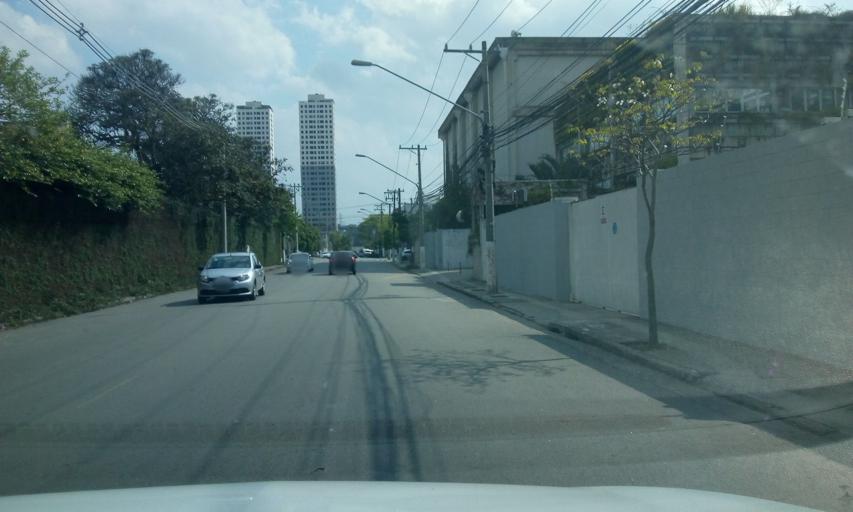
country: BR
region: Sao Paulo
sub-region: Osasco
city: Osasco
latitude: -23.5313
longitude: -46.7411
